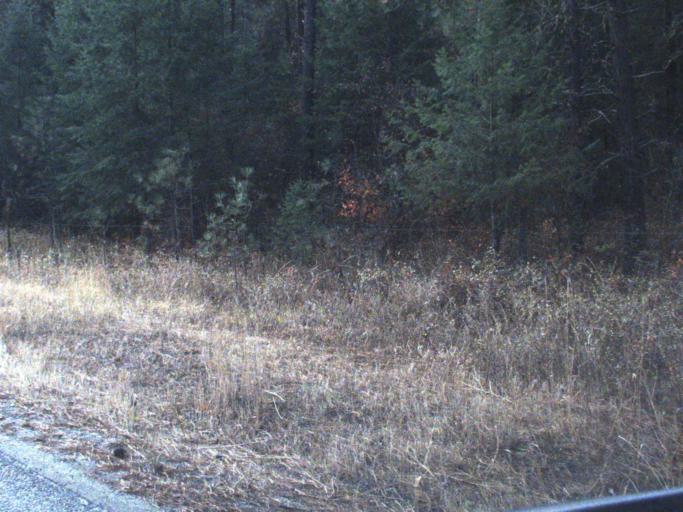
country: US
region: Washington
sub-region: Stevens County
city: Kettle Falls
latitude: 48.7703
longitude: -118.1418
